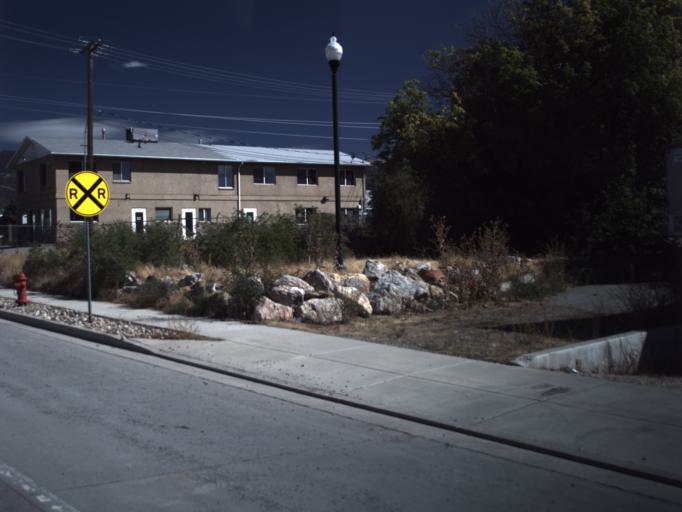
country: US
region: Utah
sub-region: Davis County
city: West Bountiful
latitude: 40.8841
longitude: -111.9100
